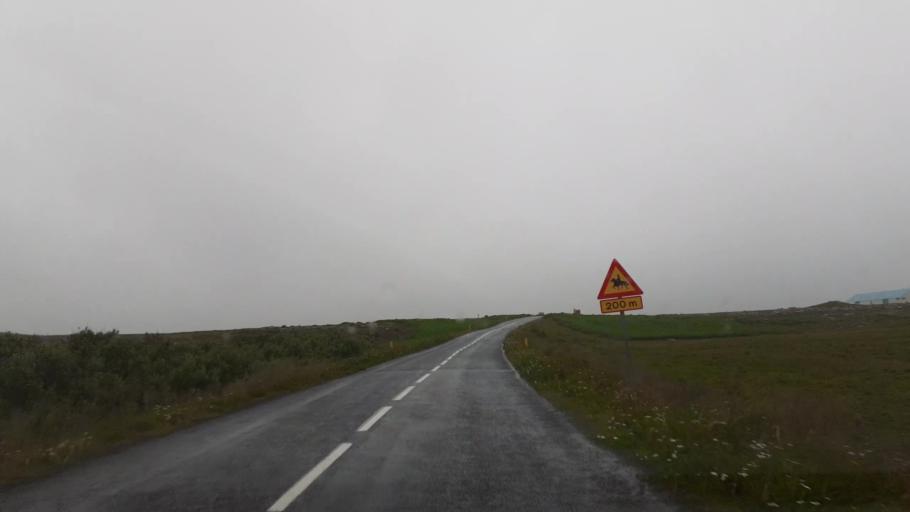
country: IS
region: Northeast
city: Husavik
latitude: 66.4588
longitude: -15.9518
